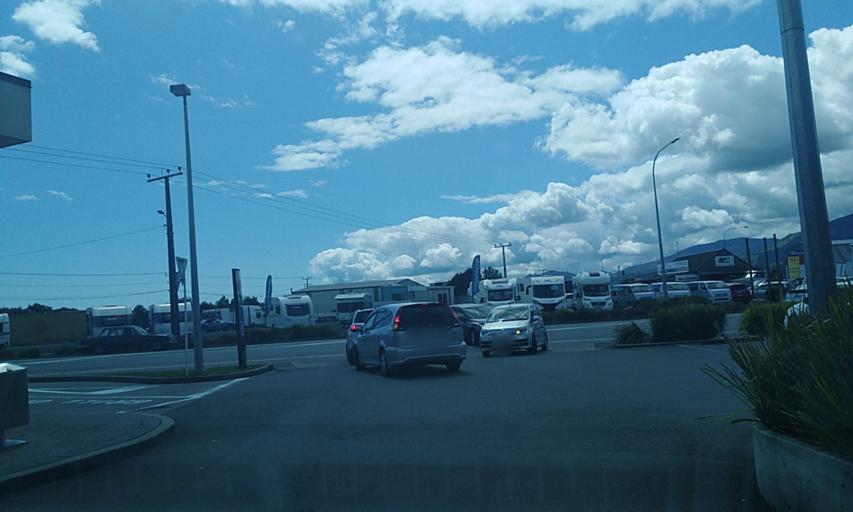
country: NZ
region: Tasman
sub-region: Tasman District
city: Richmond
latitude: -41.3364
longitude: 173.1810
